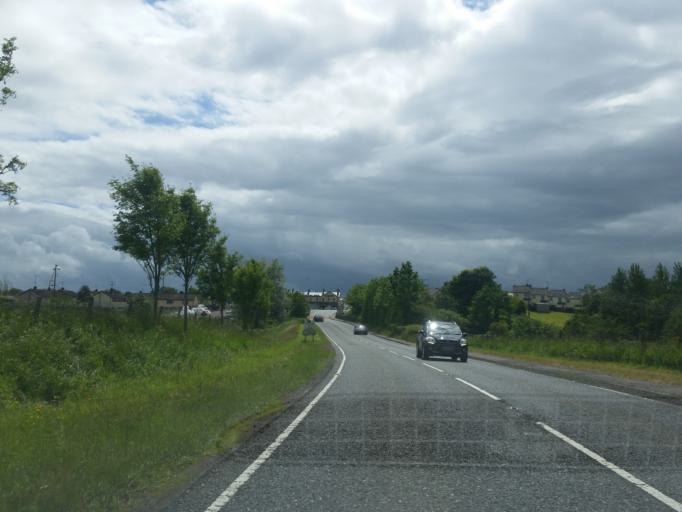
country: GB
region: Northern Ireland
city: Fivemiletown
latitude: 54.4317
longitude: -7.1290
